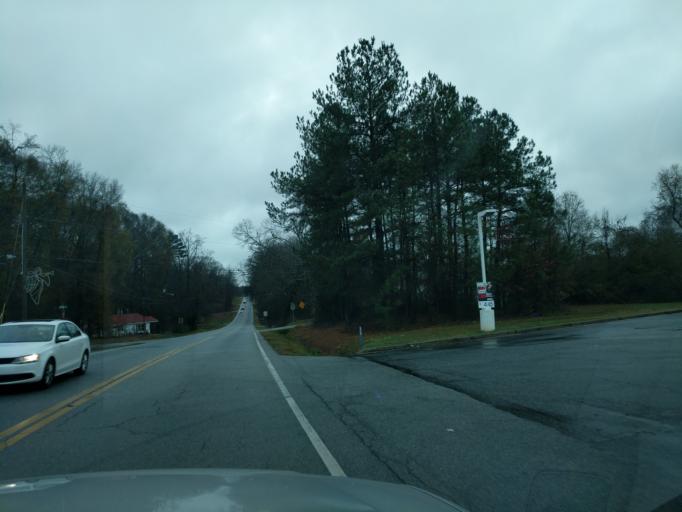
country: US
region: Georgia
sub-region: Hart County
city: Royston
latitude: 34.3433
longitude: -83.1086
